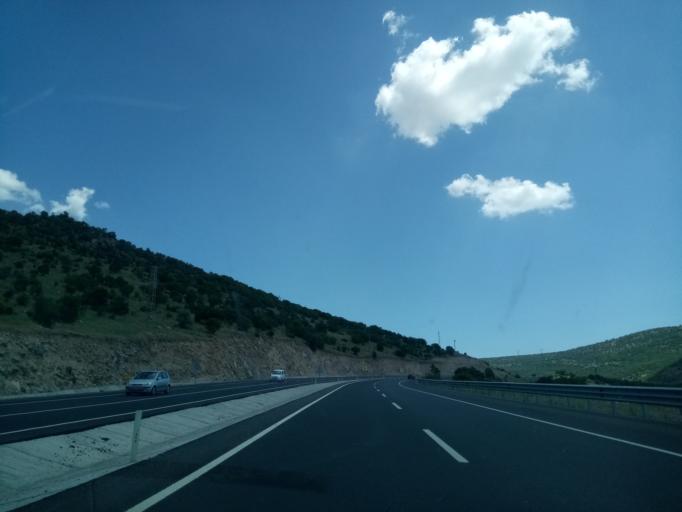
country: TR
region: Konya
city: Cavus
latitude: 37.6798
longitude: 32.0065
